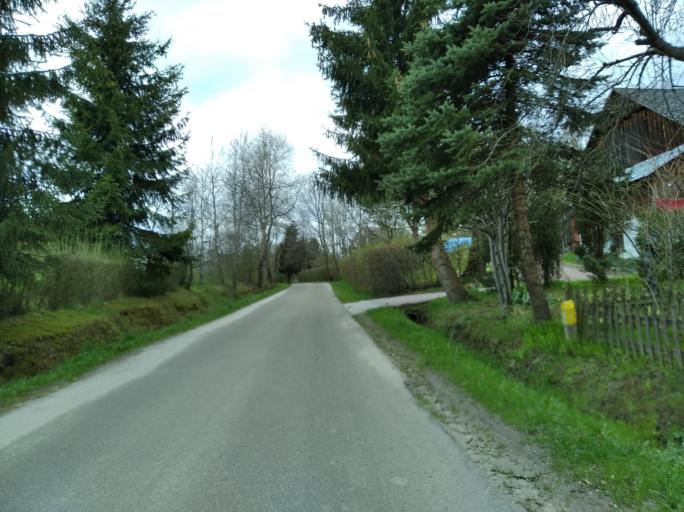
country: PL
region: Subcarpathian Voivodeship
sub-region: Powiat strzyzowski
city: Niebylec
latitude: 49.8812
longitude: 21.9148
